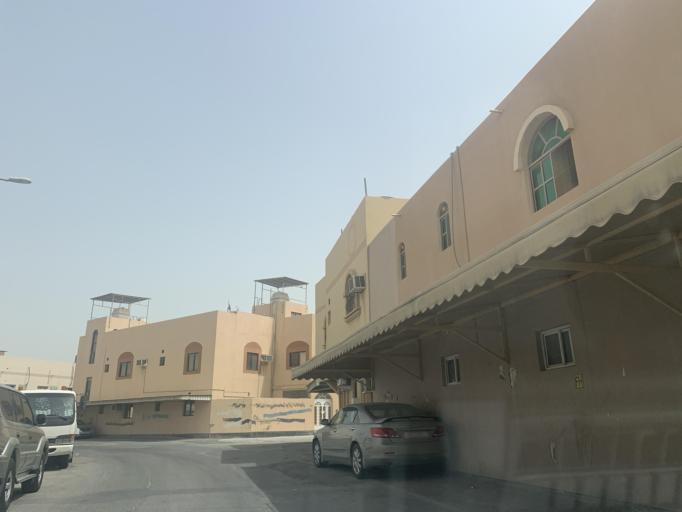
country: BH
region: Northern
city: Madinat `Isa
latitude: 26.1570
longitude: 50.5738
